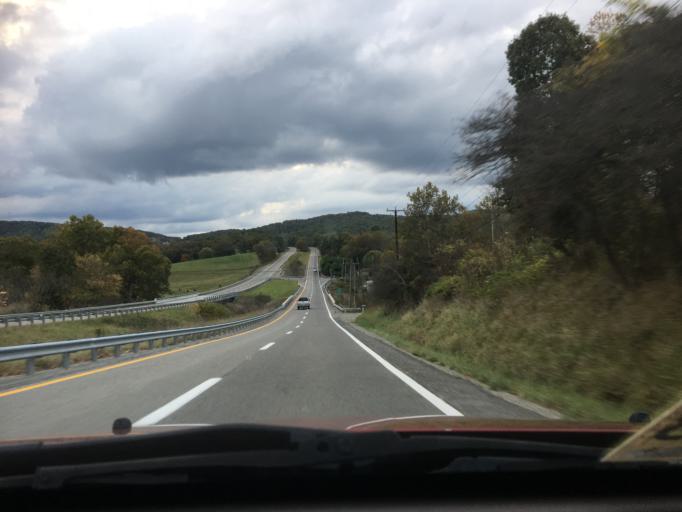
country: US
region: Virginia
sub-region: Pulaski County
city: Dublin
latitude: 37.1659
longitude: -80.7011
